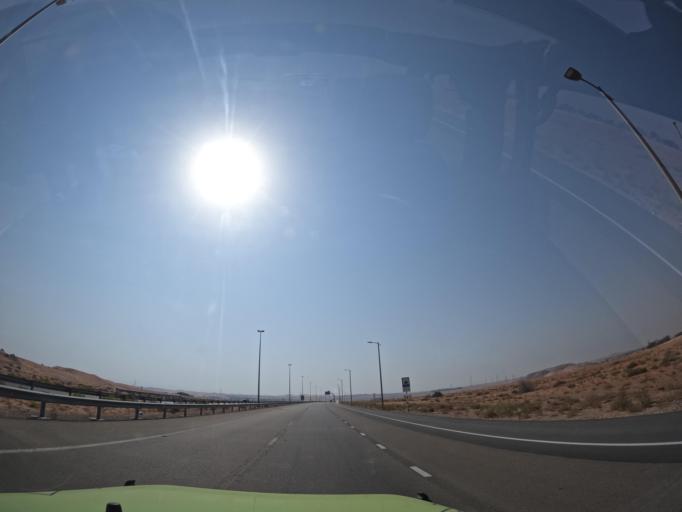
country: OM
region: Al Buraimi
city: Al Buraymi
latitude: 24.3975
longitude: 55.7179
